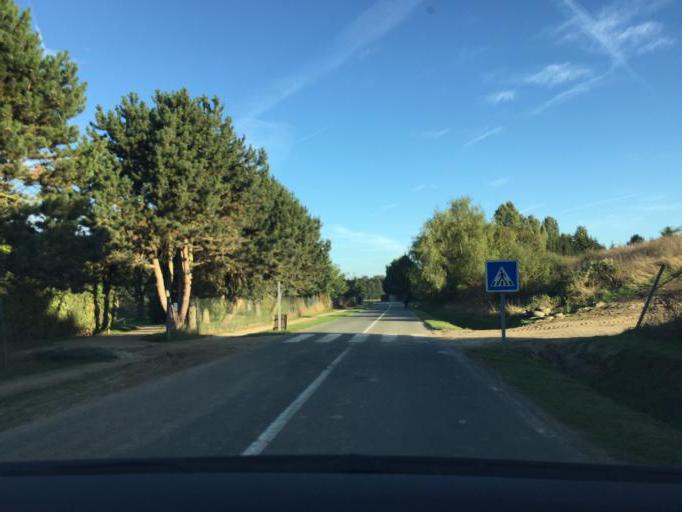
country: FR
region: Ile-de-France
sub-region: Departement de l'Essonne
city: Villiers-le-Bacle
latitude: 48.7190
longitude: 2.1384
